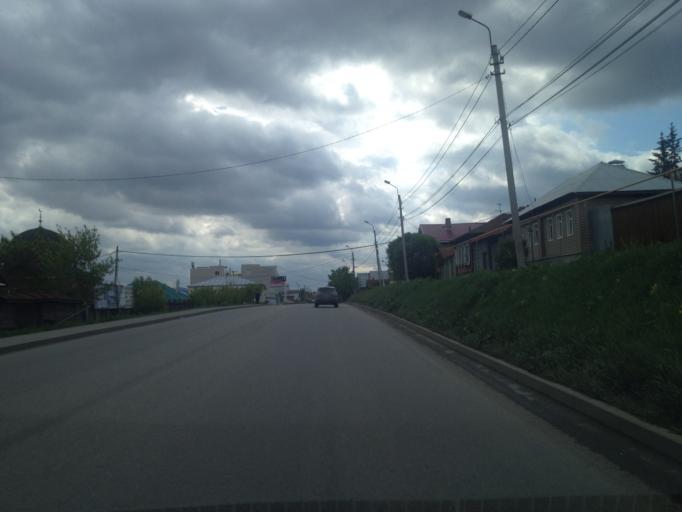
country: RU
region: Sverdlovsk
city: Istok
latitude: 56.7456
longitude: 60.6906
